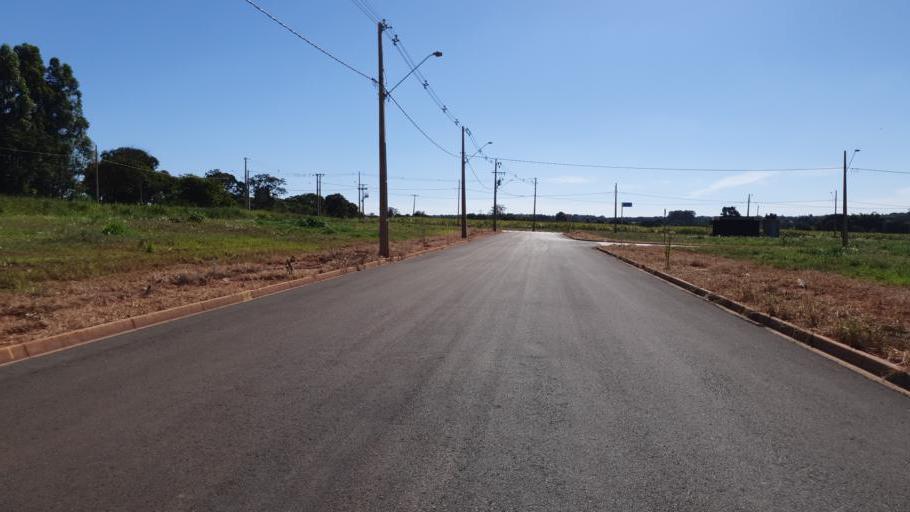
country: BR
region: Sao Paulo
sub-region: Paraguacu Paulista
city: Paraguacu Paulista
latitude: -22.4005
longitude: -50.5787
